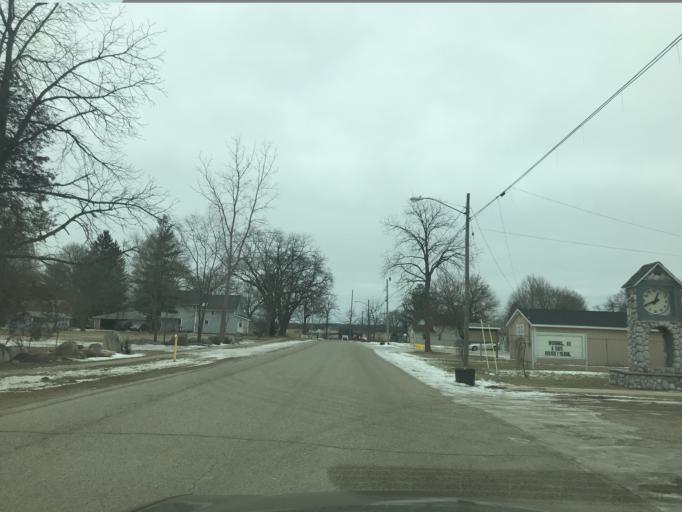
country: US
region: Michigan
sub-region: Jackson County
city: Brooklyn
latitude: 42.0699
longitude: -84.3283
